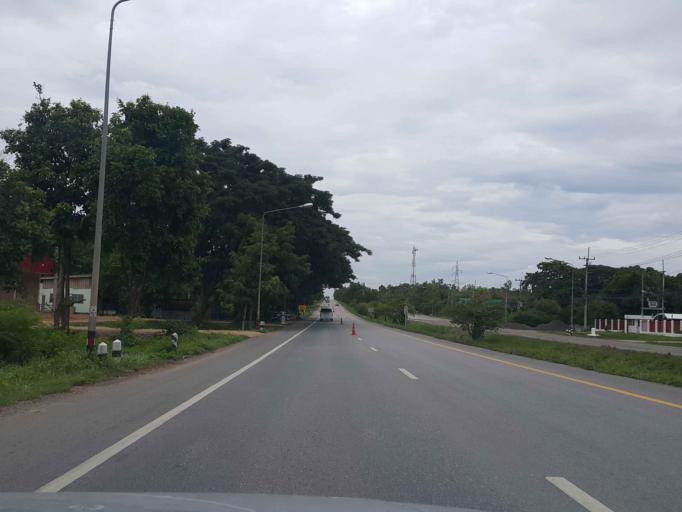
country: TH
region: Lampang
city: Thoen
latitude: 17.6125
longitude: 99.2295
